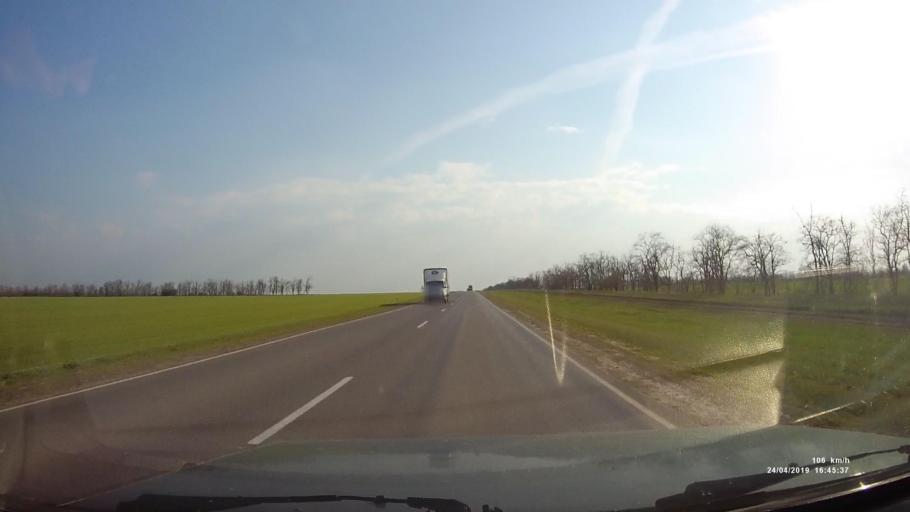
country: RU
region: Rostov
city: Gundorovskiy
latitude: 46.7675
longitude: 41.8121
